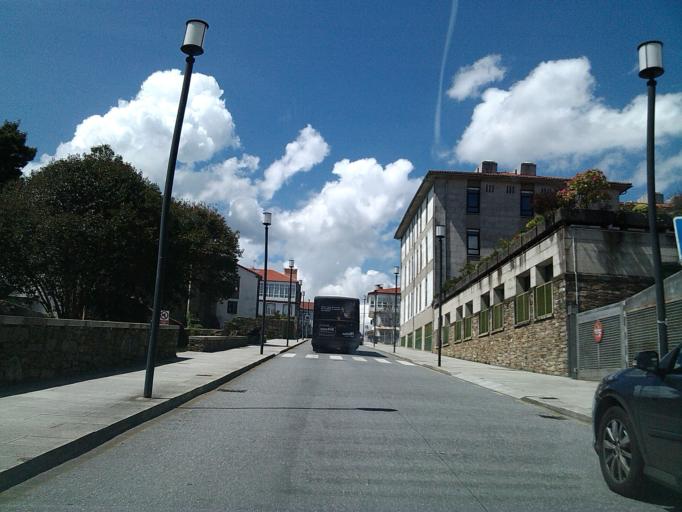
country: ES
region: Galicia
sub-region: Provincia da Coruna
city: Santiago de Compostela
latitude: 42.8834
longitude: -8.5409
